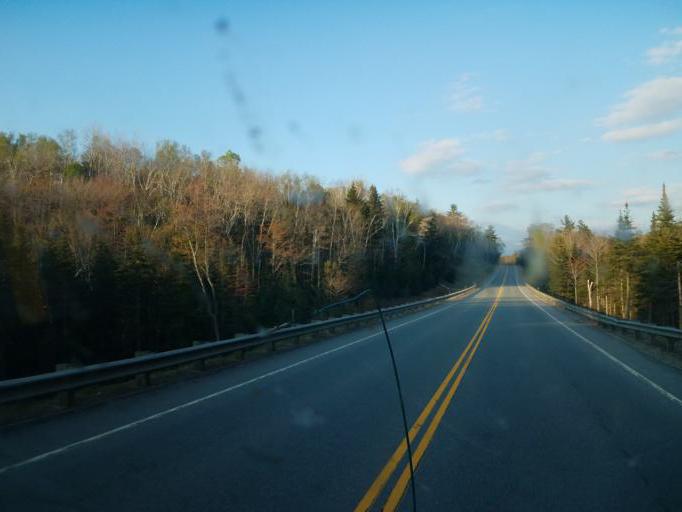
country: US
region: New Hampshire
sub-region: Grafton County
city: Deerfield
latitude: 44.2482
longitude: -71.6107
